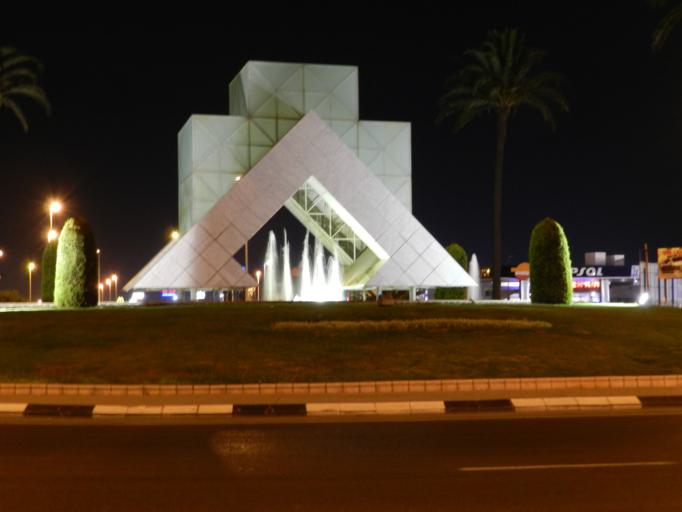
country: ES
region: Valencia
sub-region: Provincia de Alicante
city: Torrevieja
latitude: 37.9875
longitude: -0.6876
